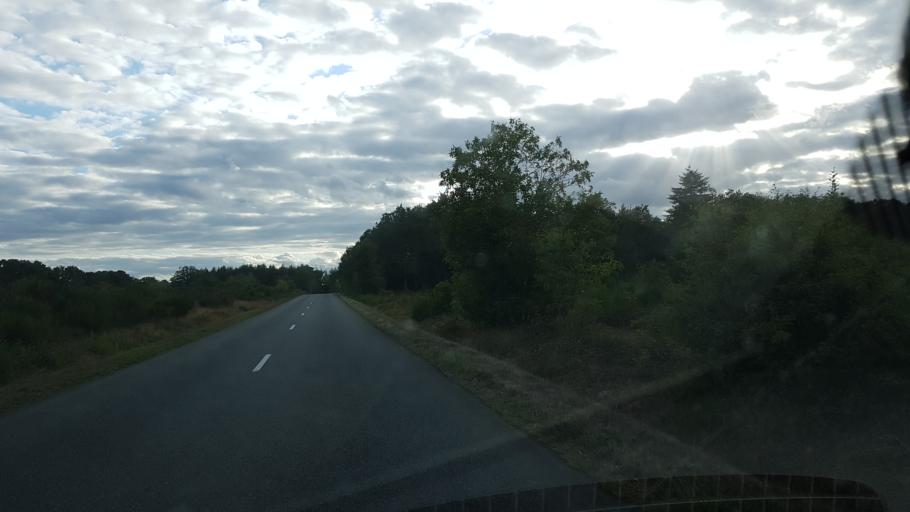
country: FR
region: Centre
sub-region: Departement du Loiret
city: Saint-Pere-sur-Loire
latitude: 47.7112
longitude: 2.3299
